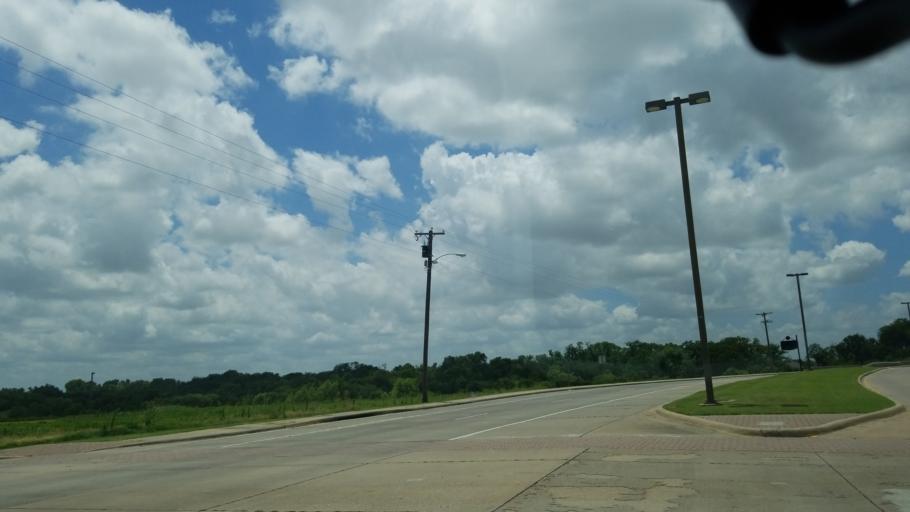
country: US
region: Texas
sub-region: Dallas County
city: Carrollton
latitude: 32.9659
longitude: -96.9402
